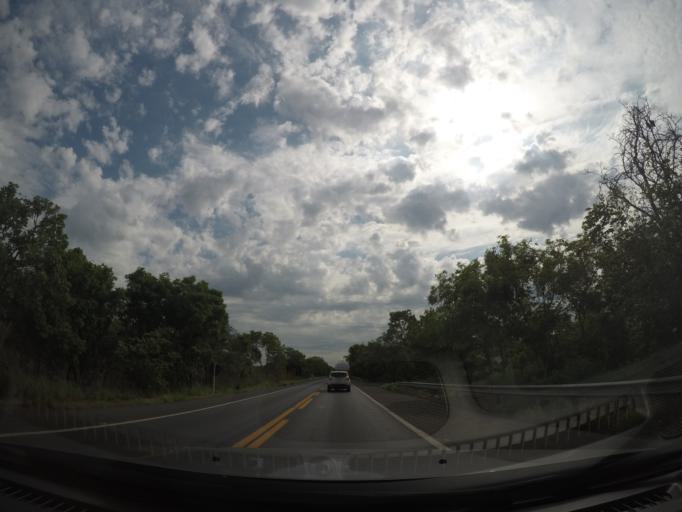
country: BR
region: Goias
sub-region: Formosa
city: Formosa
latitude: -14.9175
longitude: -46.9559
